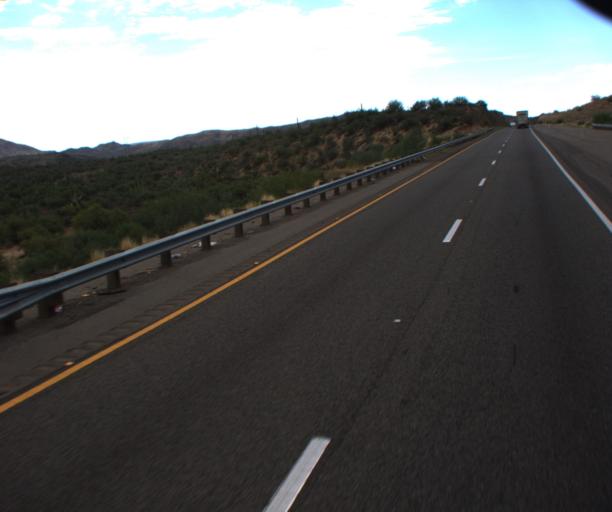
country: US
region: Arizona
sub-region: Yavapai County
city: Black Canyon City
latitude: 34.0154
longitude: -112.1471
